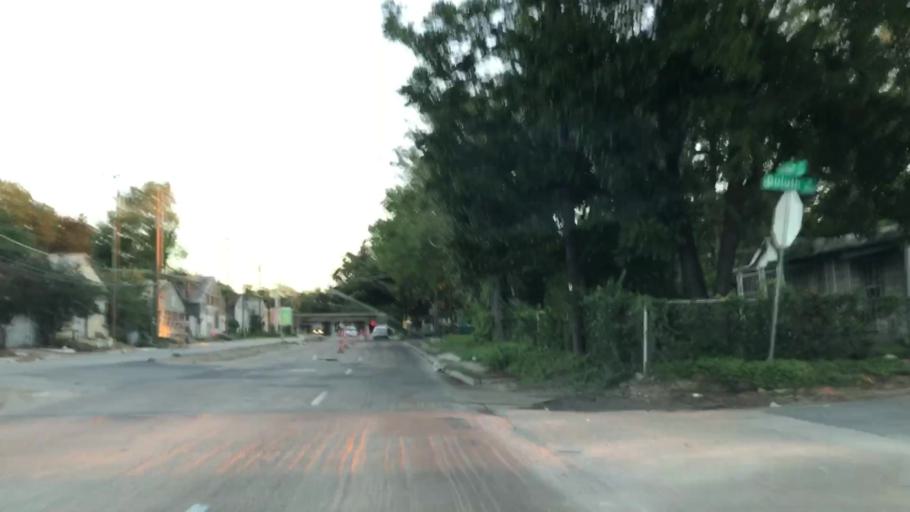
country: US
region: Texas
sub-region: Dallas County
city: Dallas
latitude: 32.7765
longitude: -96.8359
